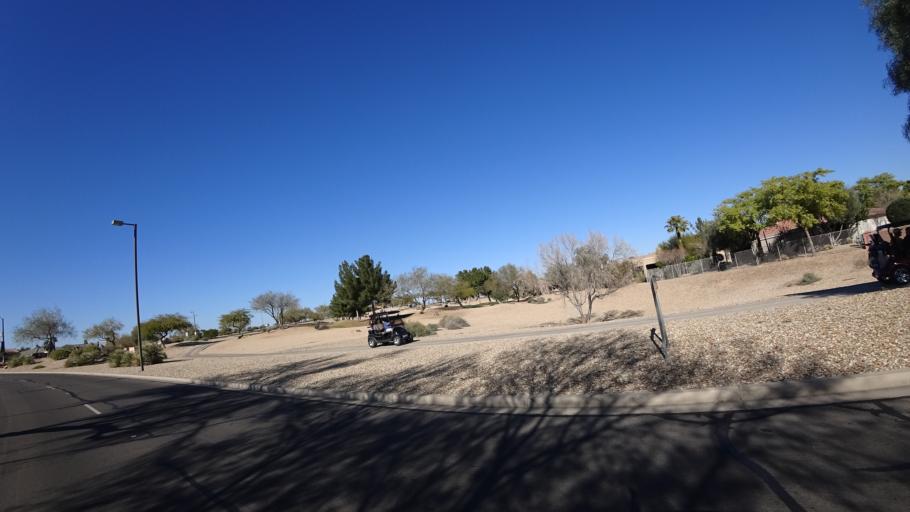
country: US
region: Arizona
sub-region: Maricopa County
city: Sun City West
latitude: 33.6654
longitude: -112.3923
